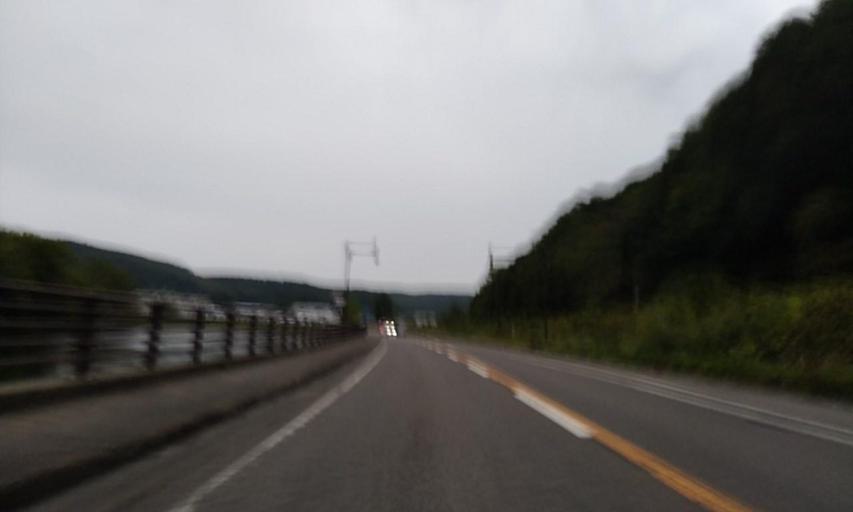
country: JP
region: Hokkaido
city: Abashiri
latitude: 44.0078
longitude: 144.2318
